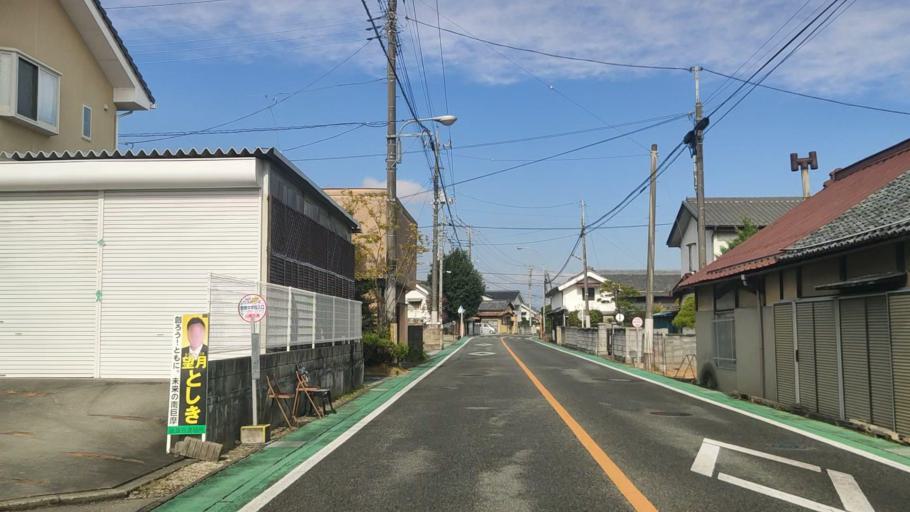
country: JP
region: Yamanashi
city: Ryuo
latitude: 35.5648
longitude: 138.4651
